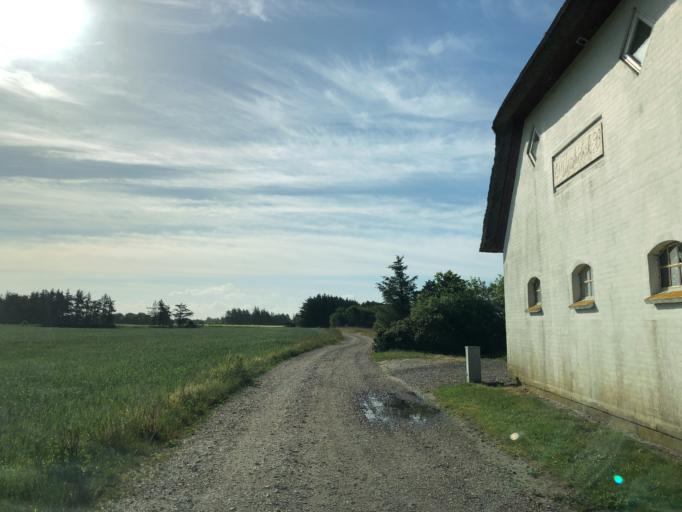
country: DK
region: Central Jutland
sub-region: Holstebro Kommune
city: Ulfborg
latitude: 56.3337
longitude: 8.2683
